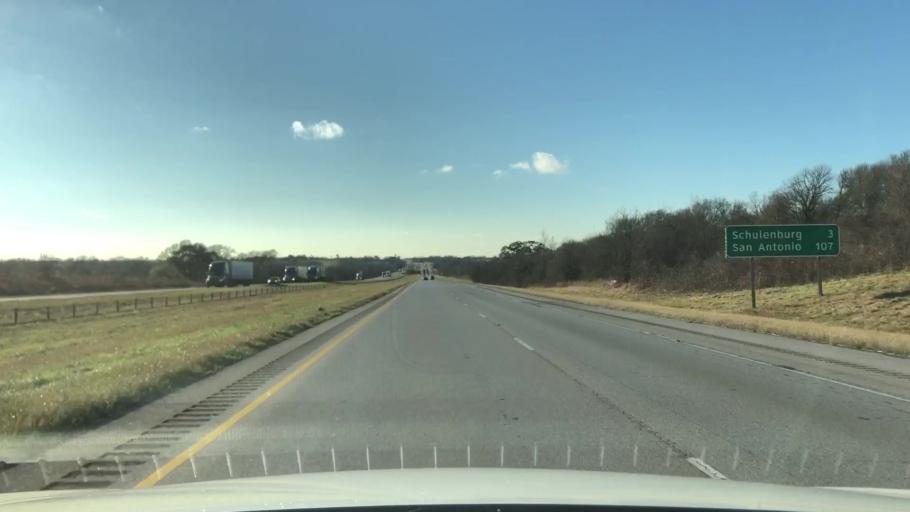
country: US
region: Texas
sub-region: Fayette County
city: Schulenburg
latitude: 29.6969
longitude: -96.8624
